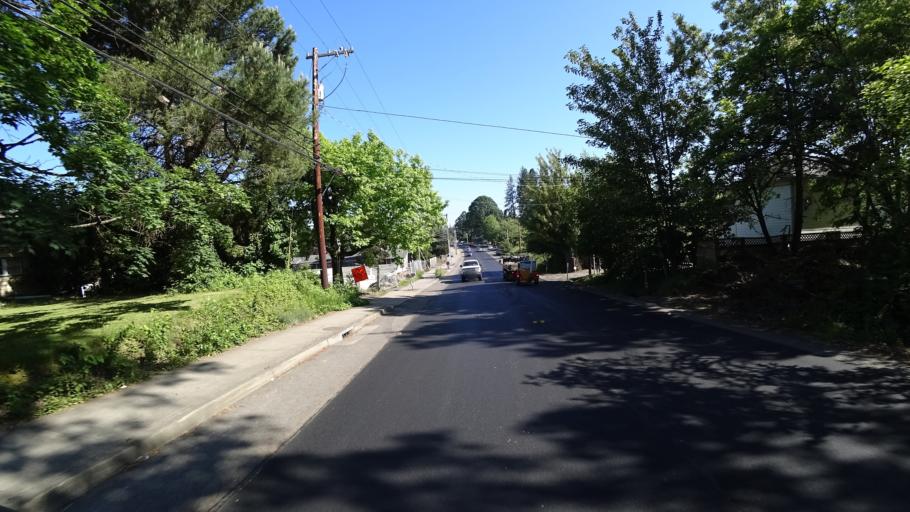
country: US
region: Oregon
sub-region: Washington County
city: Metzger
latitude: 45.4401
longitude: -122.7654
